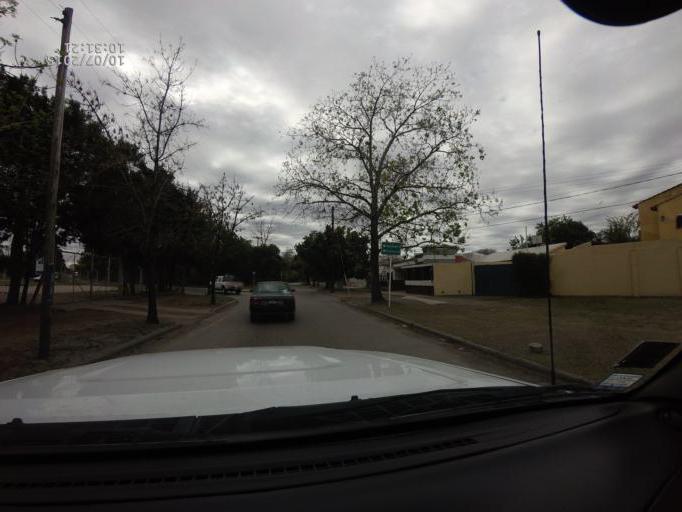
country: AR
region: Cordoba
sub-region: Departamento de Capital
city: Cordoba
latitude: -31.3562
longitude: -64.2379
